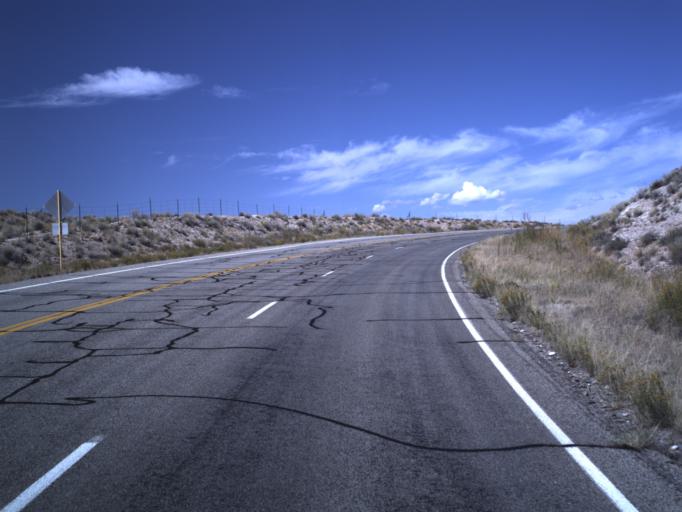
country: US
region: Utah
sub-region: San Juan County
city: Blanding
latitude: 37.2745
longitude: -109.3587
